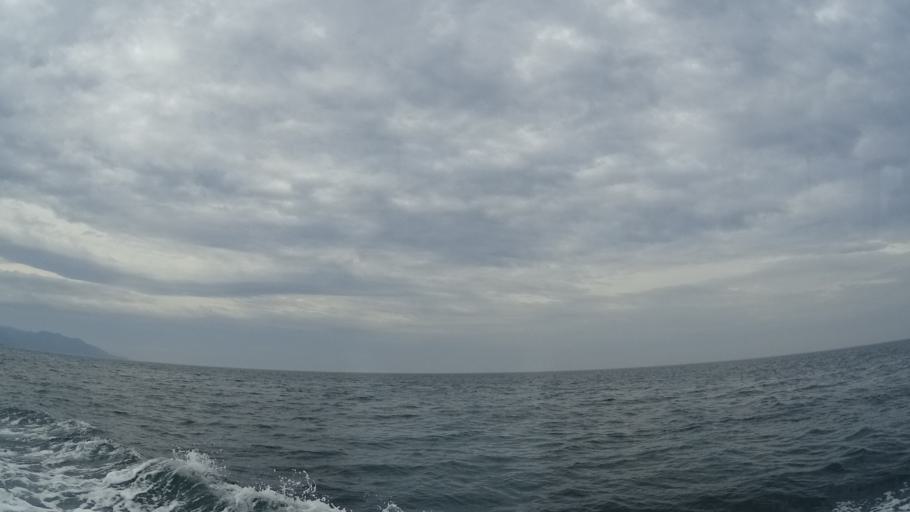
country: JP
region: Fukui
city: Mikuni
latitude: 36.2418
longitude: 136.1225
